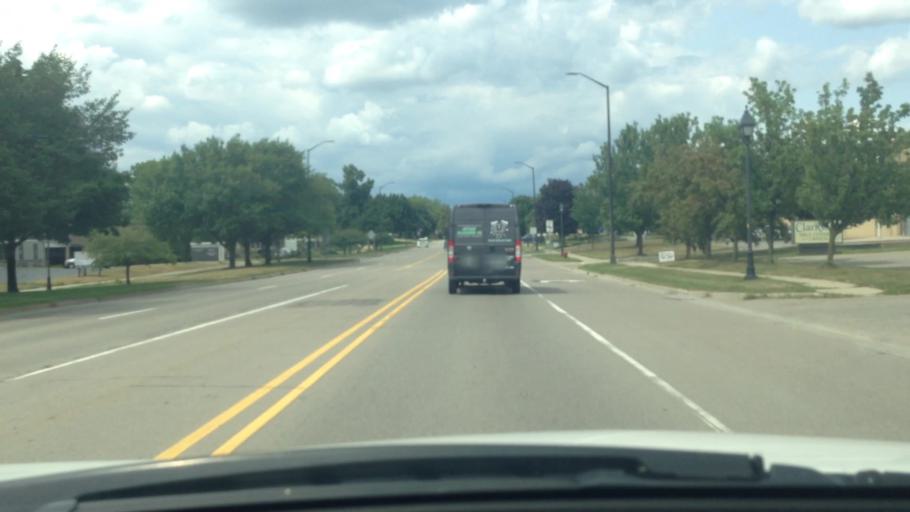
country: US
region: Michigan
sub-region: Oakland County
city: Clarkston
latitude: 42.7233
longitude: -83.4186
